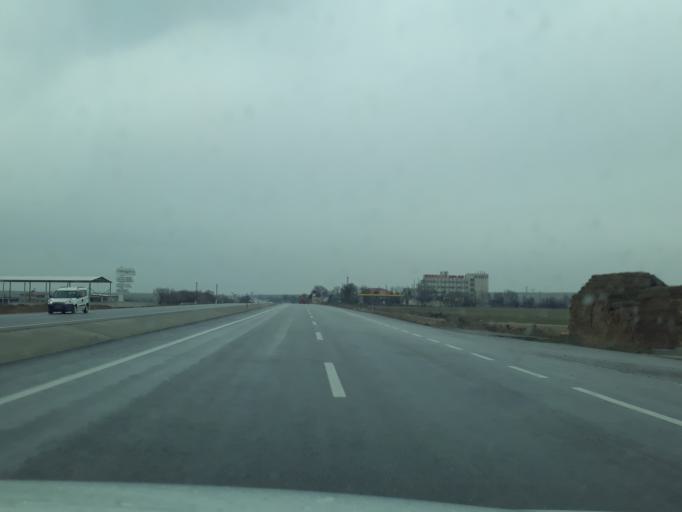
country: TR
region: Konya
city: Karapinar
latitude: 37.7165
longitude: 33.4880
